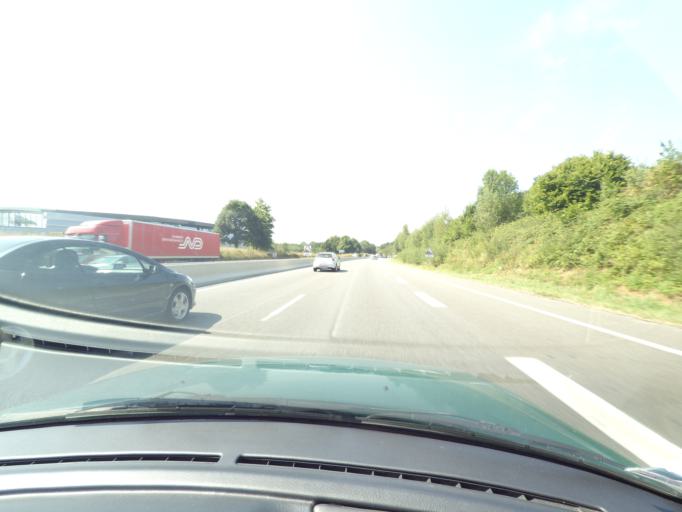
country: FR
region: Limousin
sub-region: Departement de la Haute-Vienne
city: Limoges
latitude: 45.8575
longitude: 1.2827
